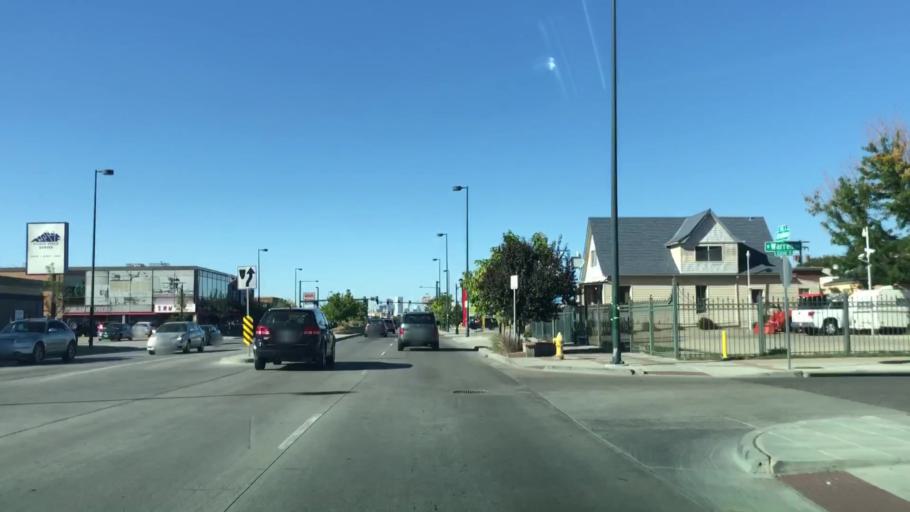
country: US
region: Colorado
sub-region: Arapahoe County
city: Englewood
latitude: 39.6765
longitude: -104.9875
